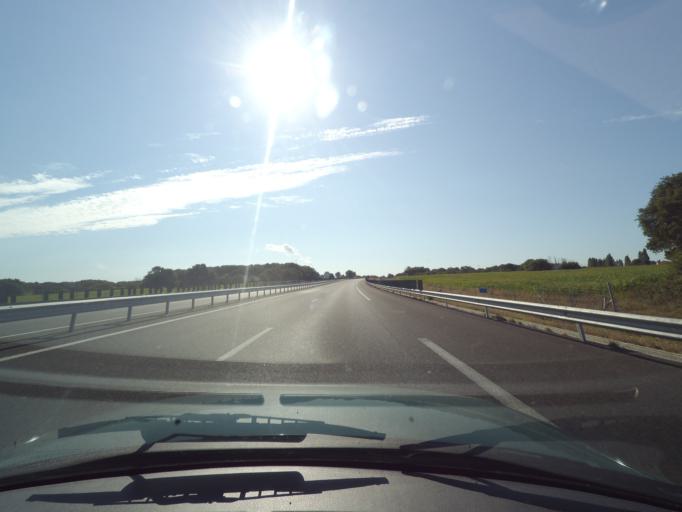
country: FR
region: Poitou-Charentes
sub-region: Departement de la Vienne
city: Terce
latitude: 46.4851
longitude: 0.5279
